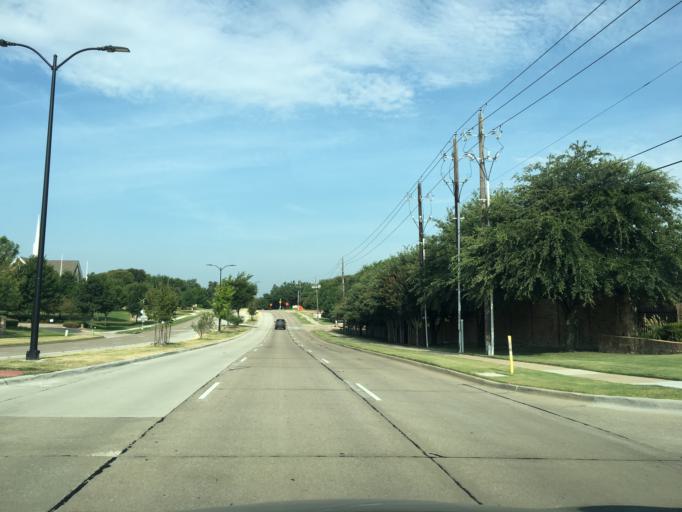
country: US
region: Texas
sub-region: Collin County
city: Fairview
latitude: 33.1988
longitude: -96.6925
